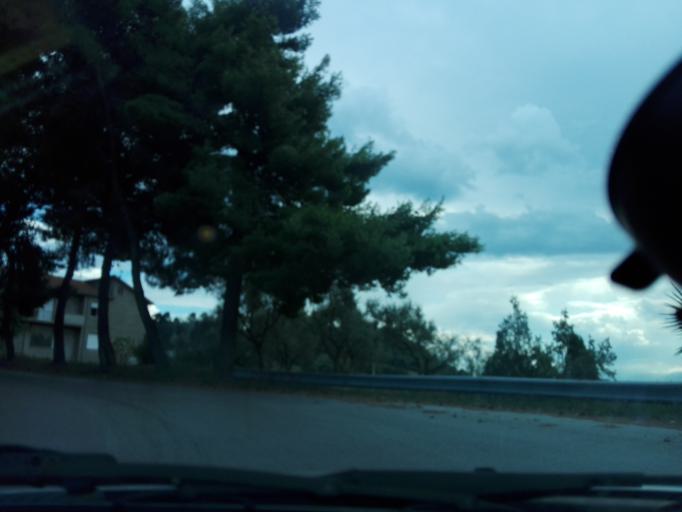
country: IT
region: Abruzzo
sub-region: Provincia di Pescara
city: Montesilvano Marina
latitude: 42.4976
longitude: 14.1419
